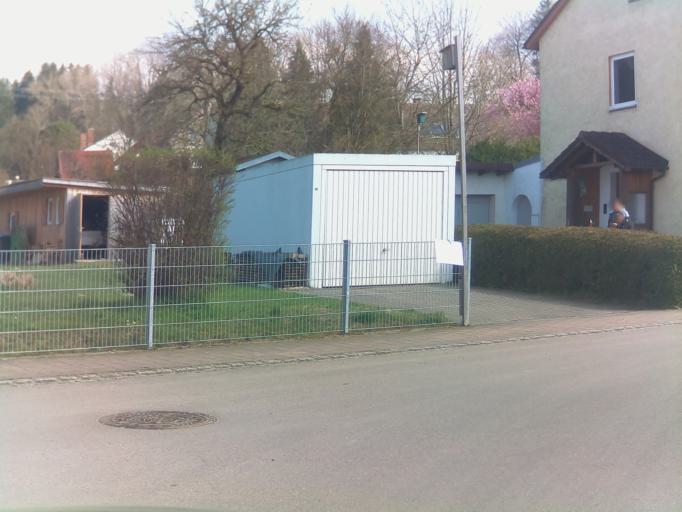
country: DE
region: Bavaria
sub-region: Swabia
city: Altenstadt
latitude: 48.1875
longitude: 10.1158
